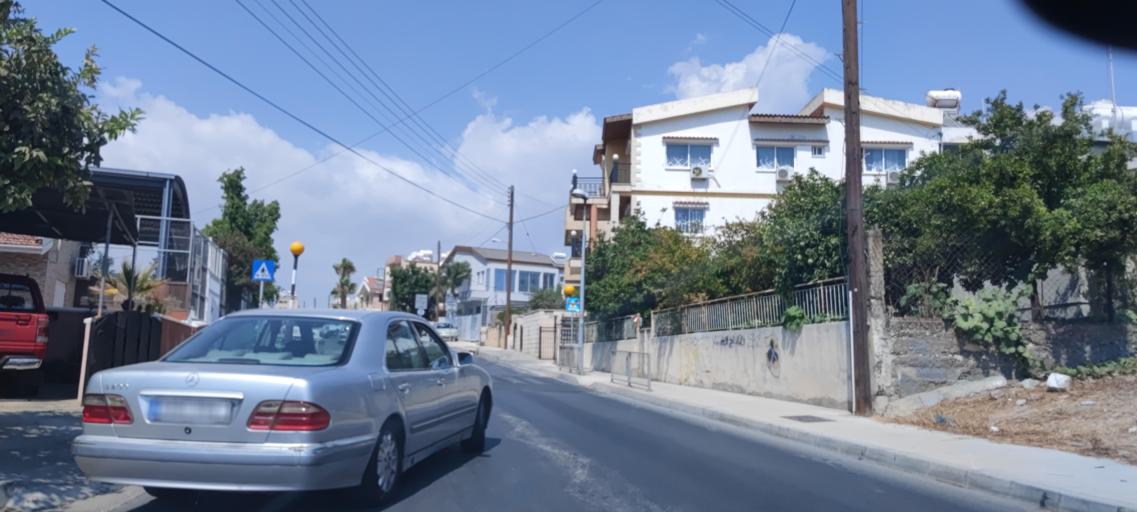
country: CY
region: Limassol
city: Limassol
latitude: 34.6935
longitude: 33.0303
